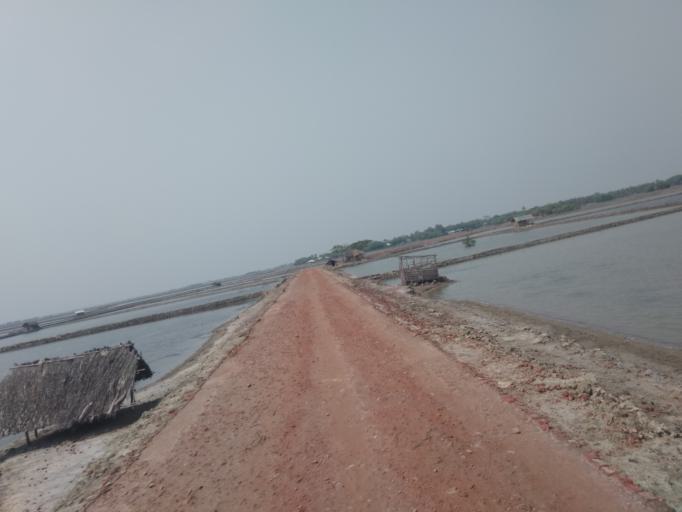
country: IN
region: West Bengal
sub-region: North 24 Parganas
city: Taki
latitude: 22.2919
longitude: 89.2714
